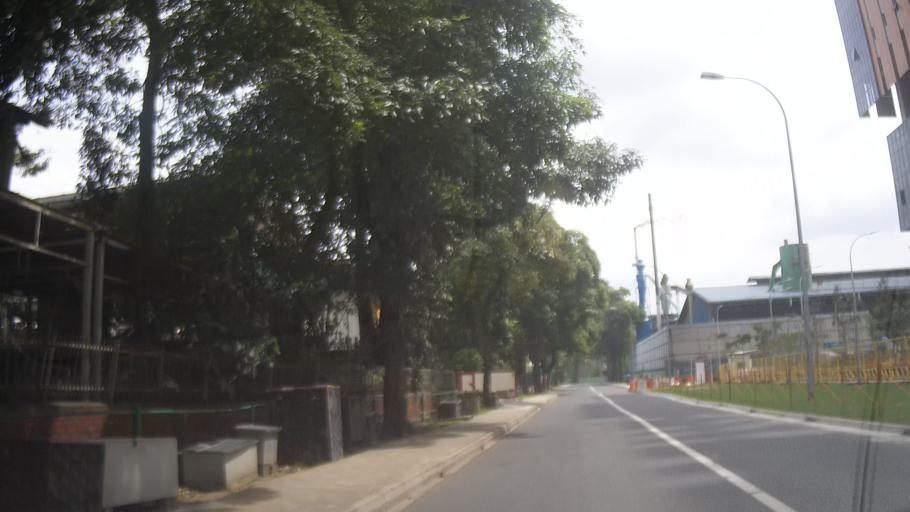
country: MY
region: Johor
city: Johor Bahru
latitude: 1.4125
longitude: 103.7499
